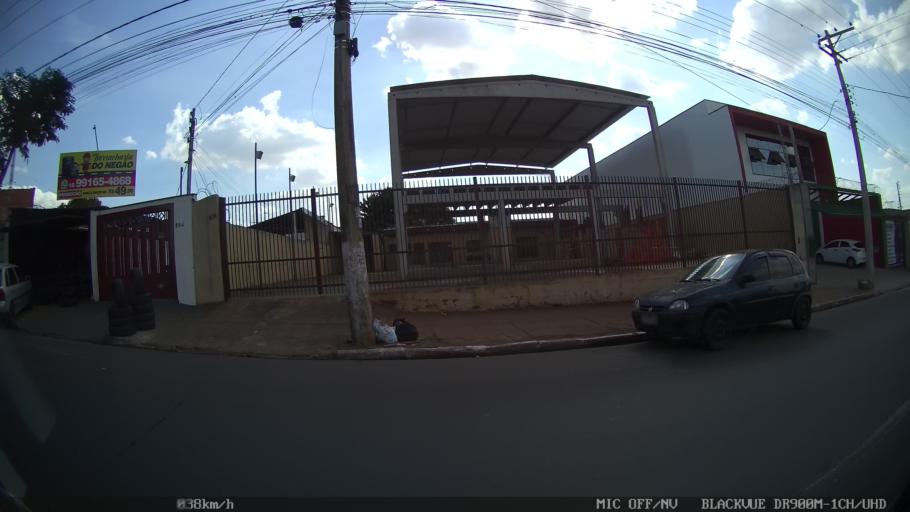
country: BR
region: Sao Paulo
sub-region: Ribeirao Preto
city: Ribeirao Preto
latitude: -21.1861
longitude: -47.8346
